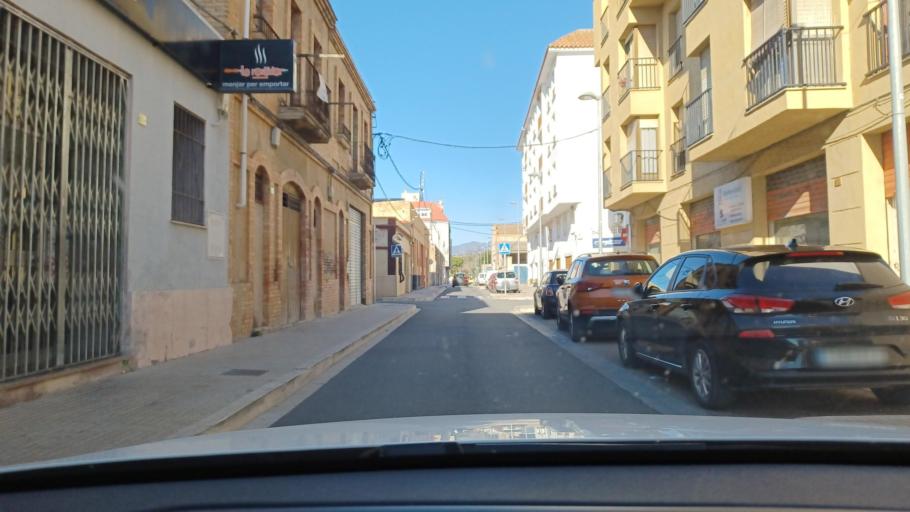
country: ES
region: Catalonia
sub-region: Provincia de Tarragona
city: Tortosa
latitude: 40.8181
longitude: 0.5233
